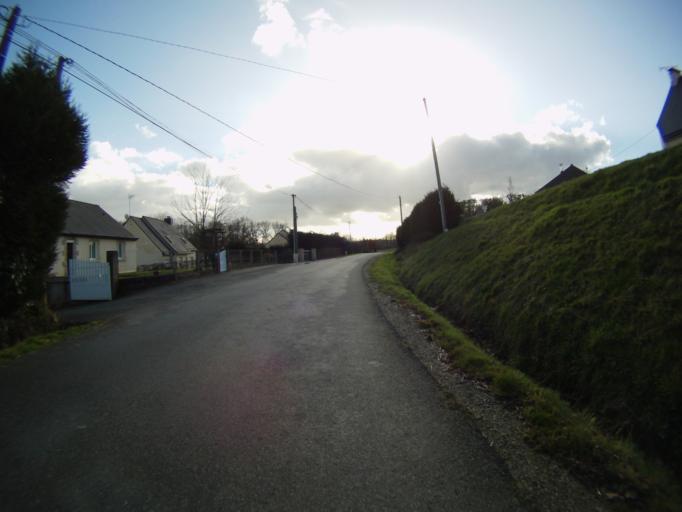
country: FR
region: Brittany
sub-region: Departement d'Ille-et-Vilaine
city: Chanteloup
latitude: 47.9319
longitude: -1.6148
